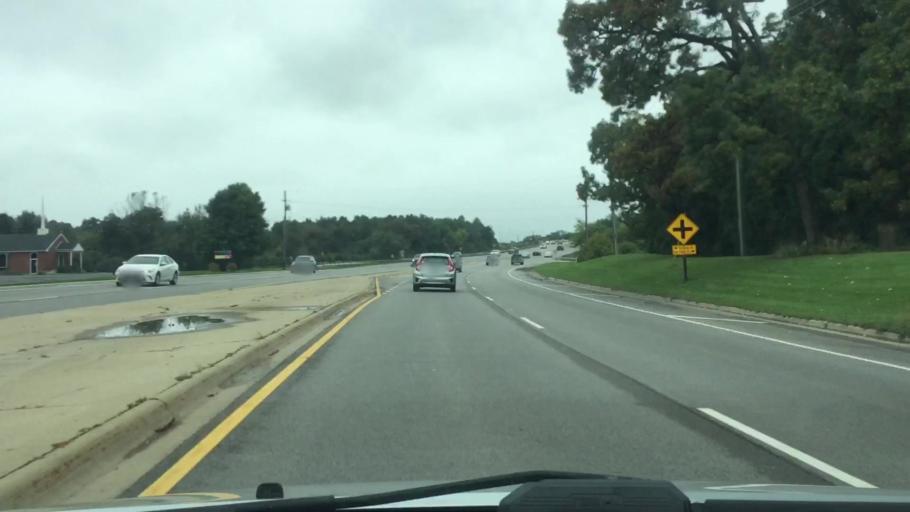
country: US
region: Illinois
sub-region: McHenry County
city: Crystal Lake
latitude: 42.2360
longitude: -88.2867
